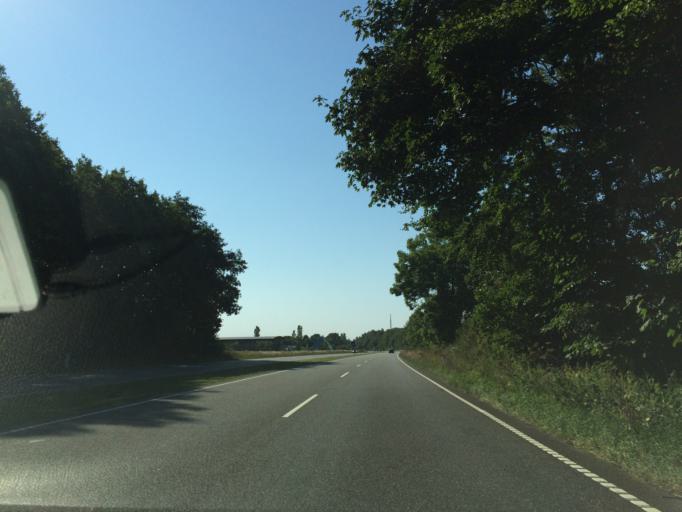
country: DK
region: South Denmark
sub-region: Kolding Kommune
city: Kolding
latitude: 55.5159
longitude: 9.5017
